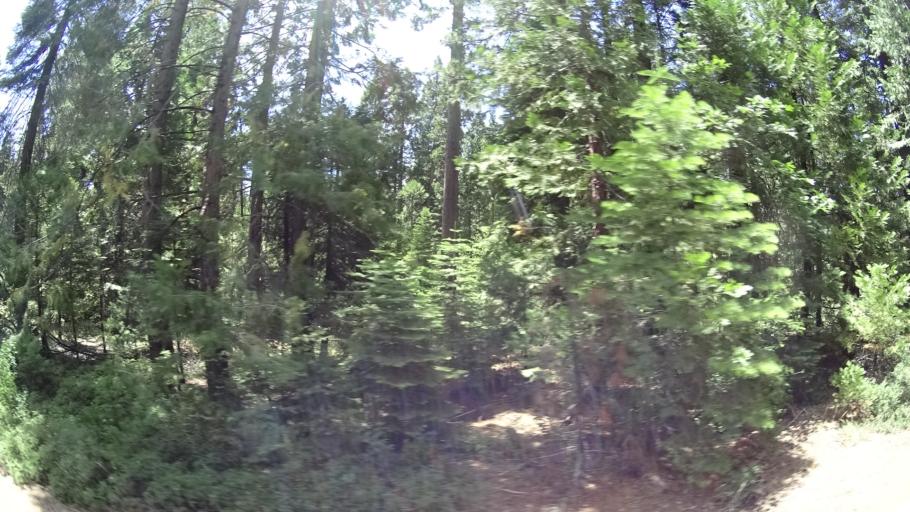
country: US
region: California
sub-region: Calaveras County
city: Arnold
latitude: 38.2967
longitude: -120.2614
